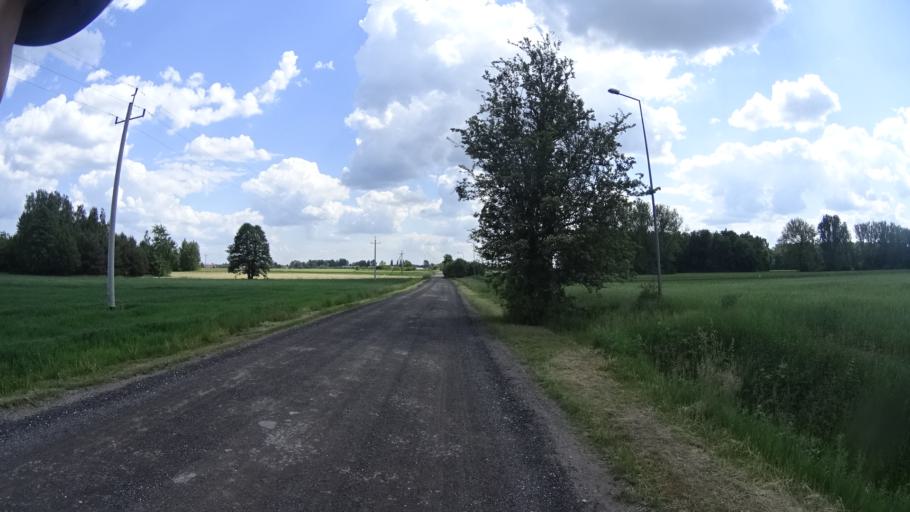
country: PL
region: Masovian Voivodeship
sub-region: Powiat pruszkowski
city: Nadarzyn
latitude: 52.0618
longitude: 20.8224
